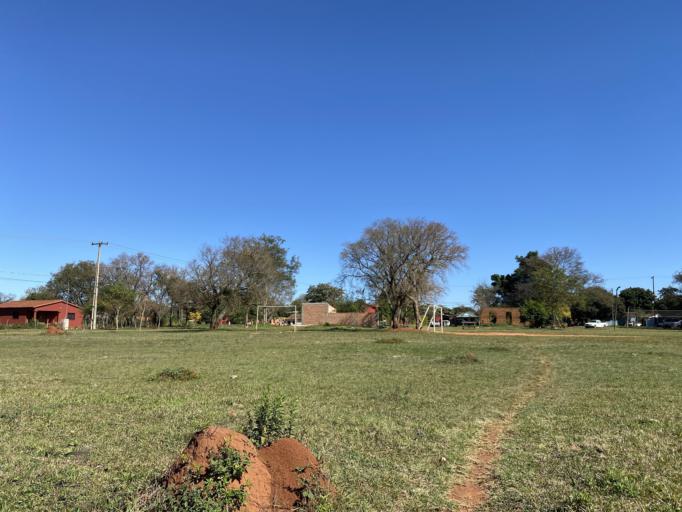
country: PY
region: Misiones
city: San Juan Bautista
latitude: -26.6751
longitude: -57.1416
